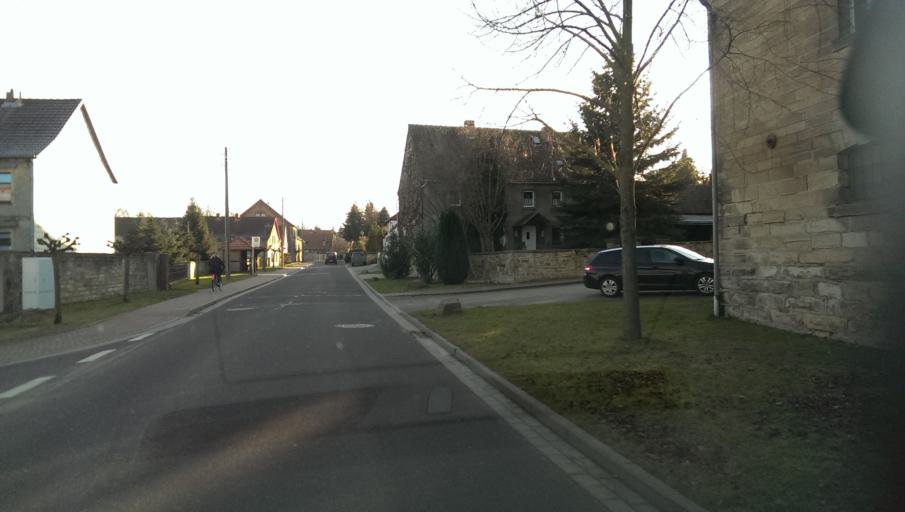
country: DE
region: Saxony-Anhalt
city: Eilsleben
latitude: 52.1337
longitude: 11.1909
